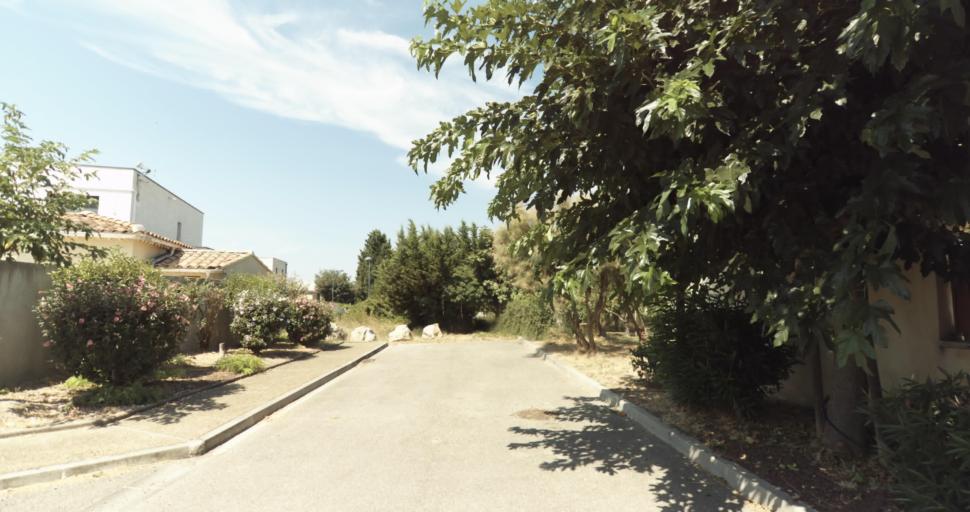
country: FR
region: Provence-Alpes-Cote d'Azur
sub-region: Departement du Vaucluse
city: Monteux
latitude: 44.0322
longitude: 4.9832
